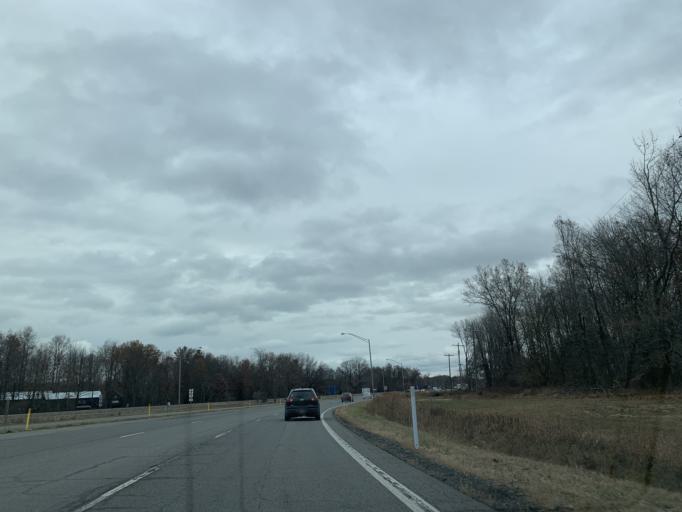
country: US
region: Indiana
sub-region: LaPorte County
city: Long Beach
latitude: 41.7456
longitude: -86.8255
